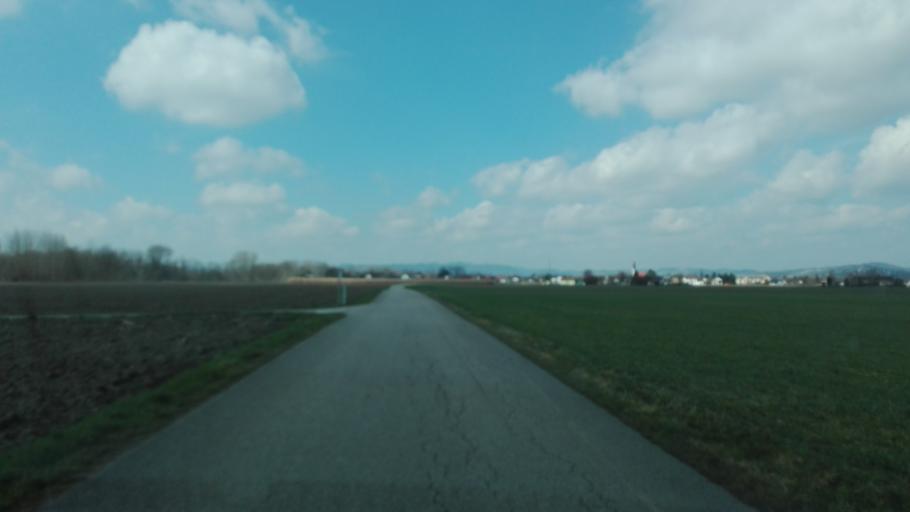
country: AT
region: Upper Austria
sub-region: Politischer Bezirk Urfahr-Umgebung
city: Goldworth
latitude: 48.3212
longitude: 14.1125
